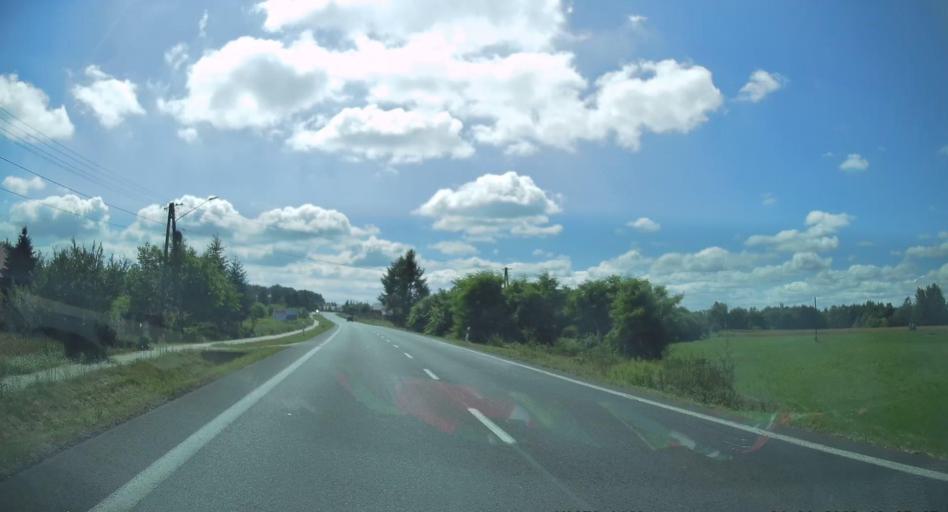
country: PL
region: Subcarpathian Voivodeship
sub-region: Powiat debicki
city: Brzeznica
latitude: 50.1248
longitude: 21.4865
